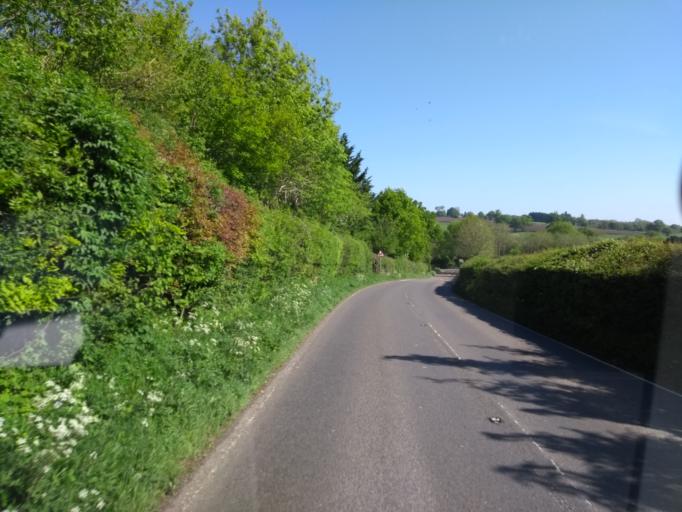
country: GB
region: England
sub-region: Devon
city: Axminster
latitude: 50.8143
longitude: -2.9742
